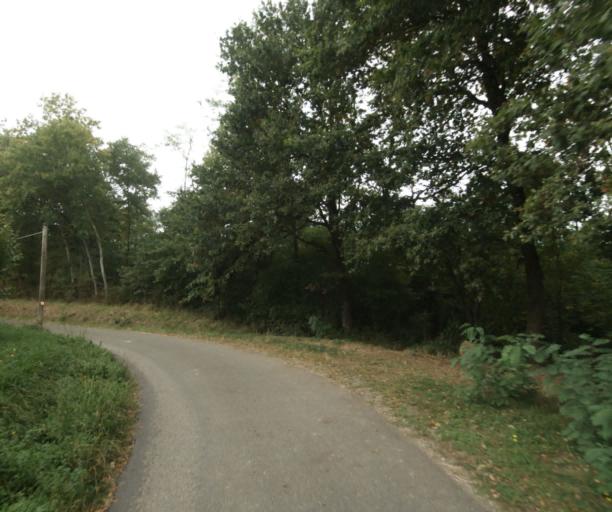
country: FR
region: Midi-Pyrenees
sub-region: Departement du Gers
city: Eauze
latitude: 43.8857
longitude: 0.1095
